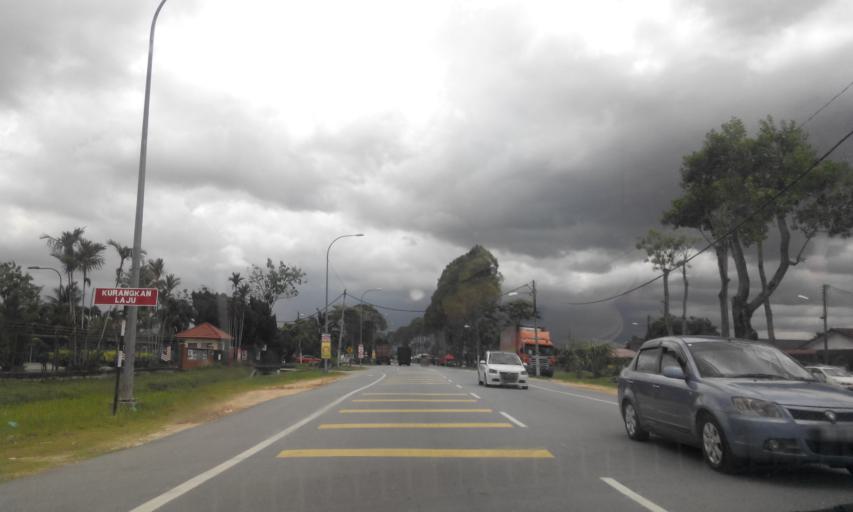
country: MY
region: Perak
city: Parit Buntar
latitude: 5.1097
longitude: 100.4889
